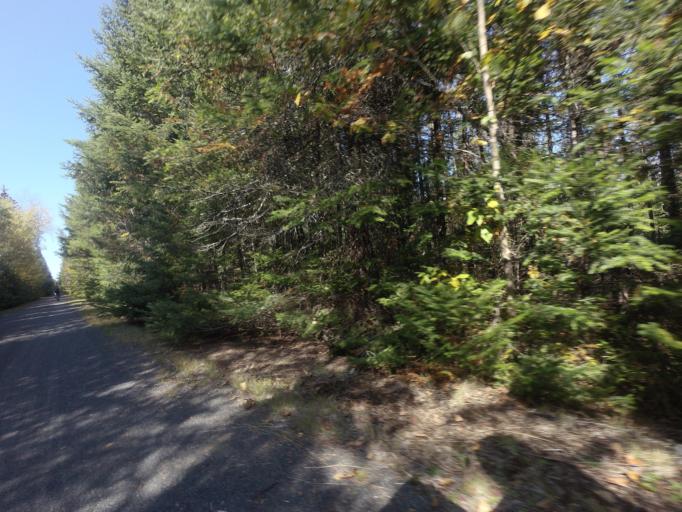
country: CA
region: Quebec
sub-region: Laurentides
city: Sainte-Agathe-des-Monts
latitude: 46.0940
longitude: -74.3486
